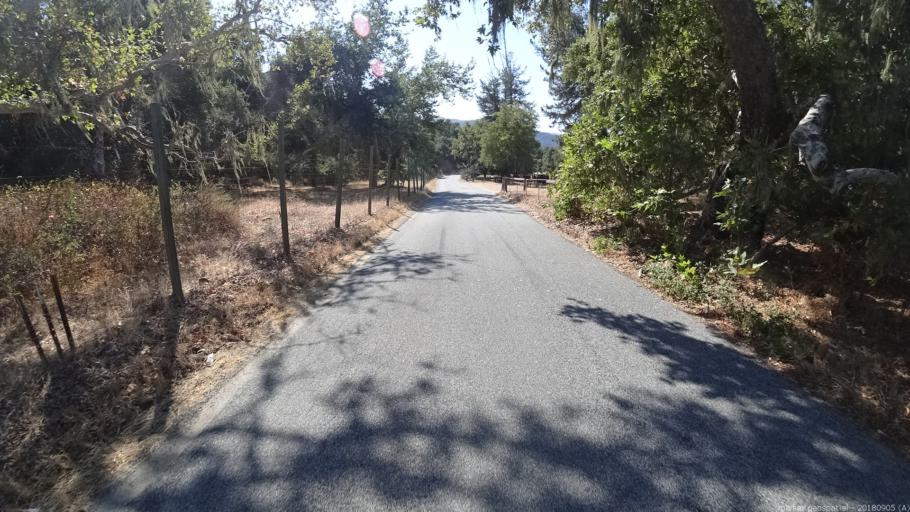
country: US
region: California
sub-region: Monterey County
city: Carmel Valley Village
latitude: 36.4077
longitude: -121.6648
